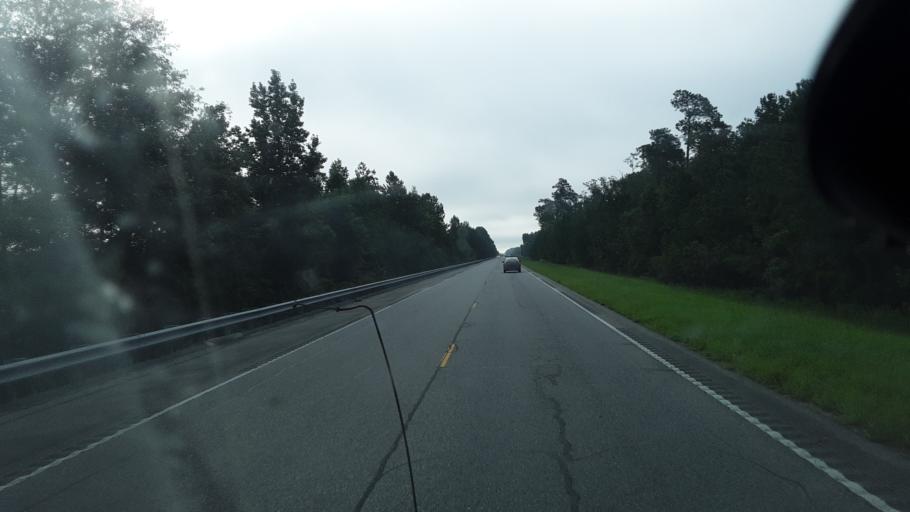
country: US
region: South Carolina
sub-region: Florence County
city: Johnsonville
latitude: 33.8558
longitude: -79.3090
